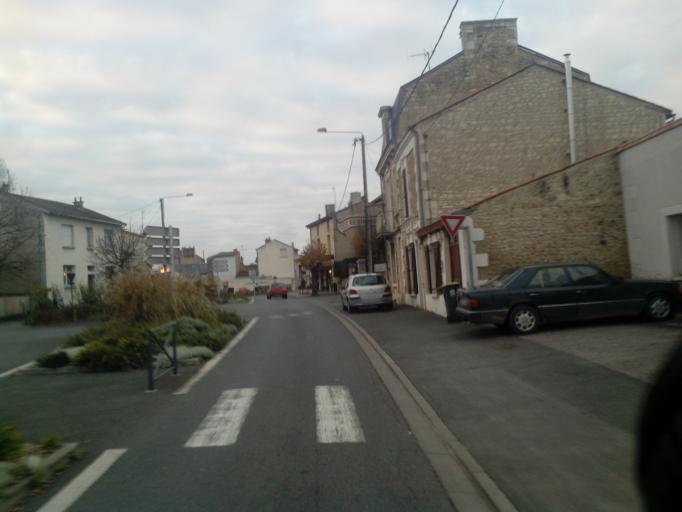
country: FR
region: Poitou-Charentes
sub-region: Departement de la Vienne
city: Saint-Benoit
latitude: 46.5728
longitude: 0.3677
